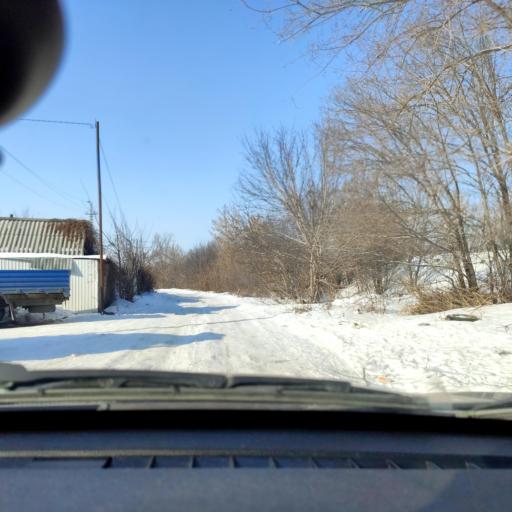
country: RU
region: Samara
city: Tol'yatti
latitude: 53.5696
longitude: 49.4555
